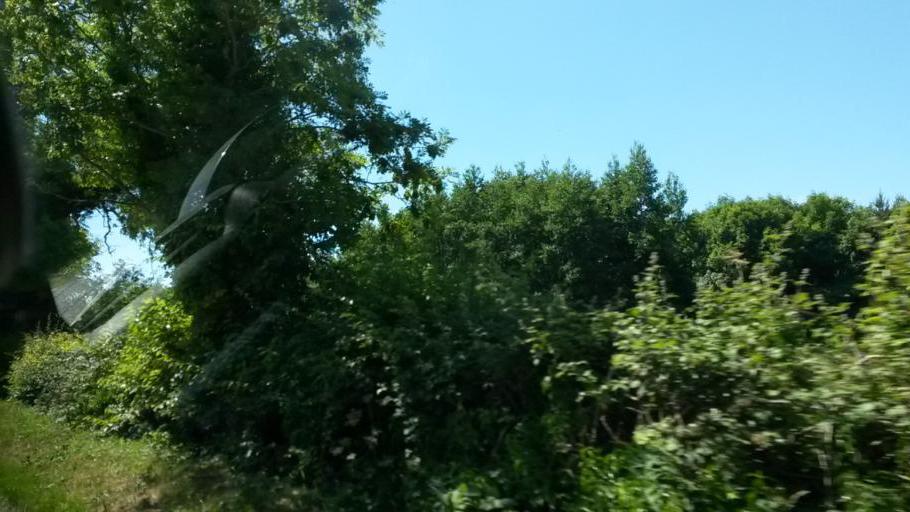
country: IE
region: Leinster
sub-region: Fingal County
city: Swords
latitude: 53.4832
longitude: -6.2710
